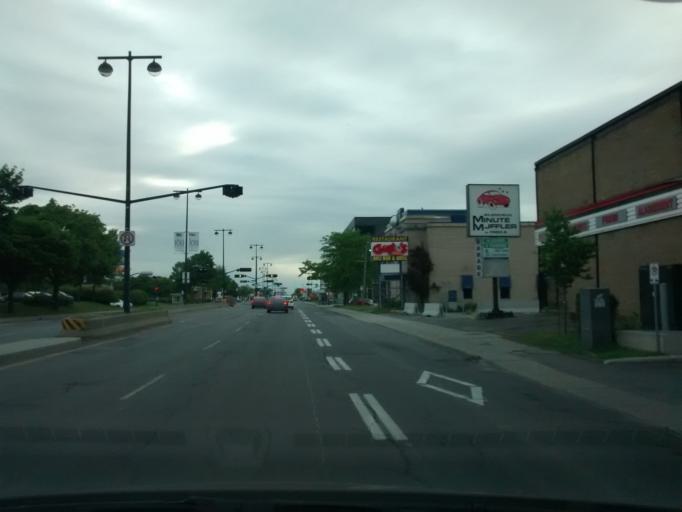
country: CA
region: Quebec
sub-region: Montreal
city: Saint-Leonard
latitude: 45.5844
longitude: -73.6304
